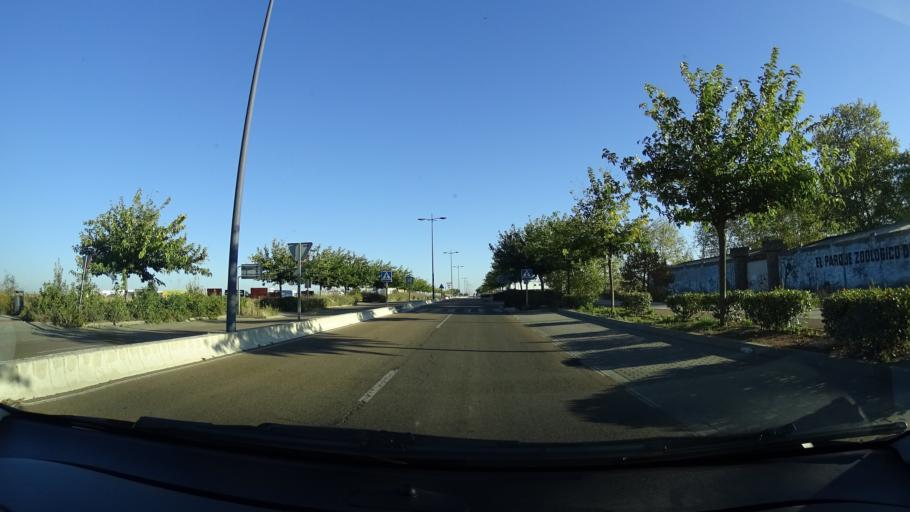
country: ES
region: Extremadura
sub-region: Provincia de Badajoz
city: Almendralejo
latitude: 38.7059
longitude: -6.4008
